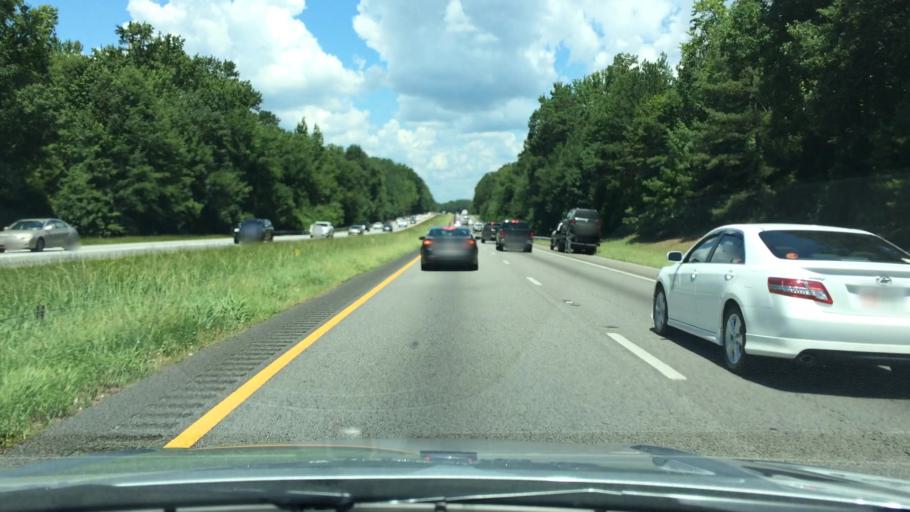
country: US
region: South Carolina
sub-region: Lexington County
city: Irmo
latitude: 34.1245
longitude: -81.2011
